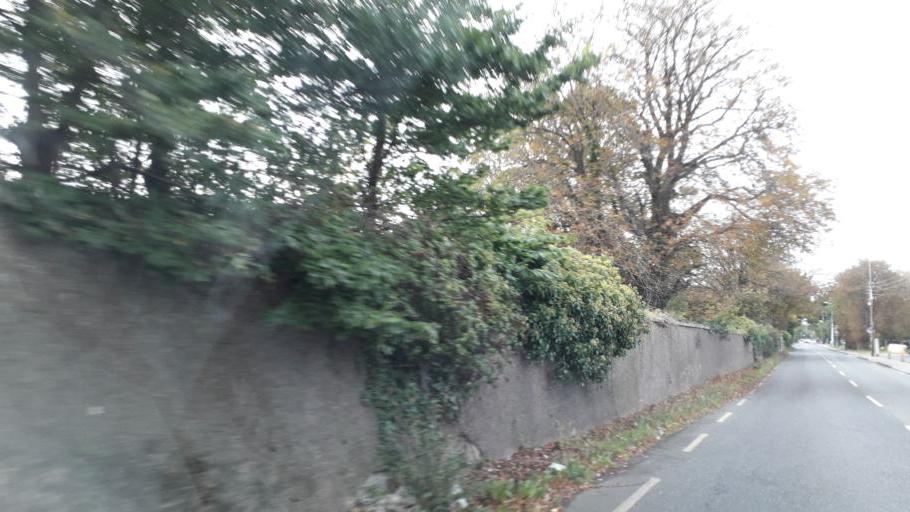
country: IE
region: Leinster
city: Cabinteely
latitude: 53.2768
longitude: -6.1529
